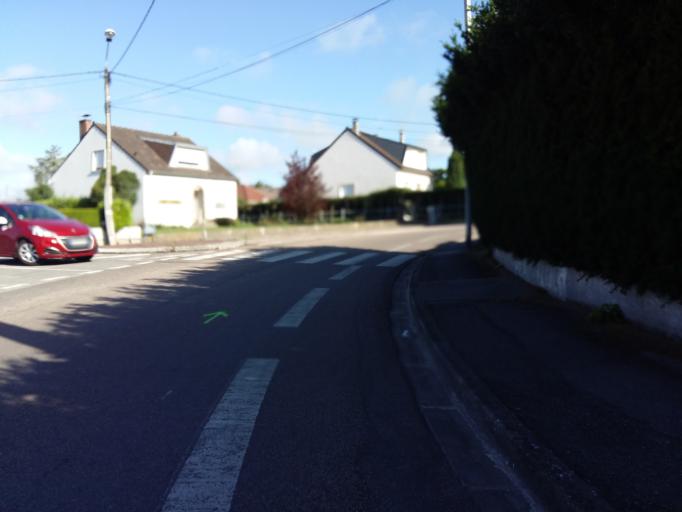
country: FR
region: Picardie
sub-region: Departement de la Somme
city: Rivery
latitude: 49.9060
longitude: 2.3265
